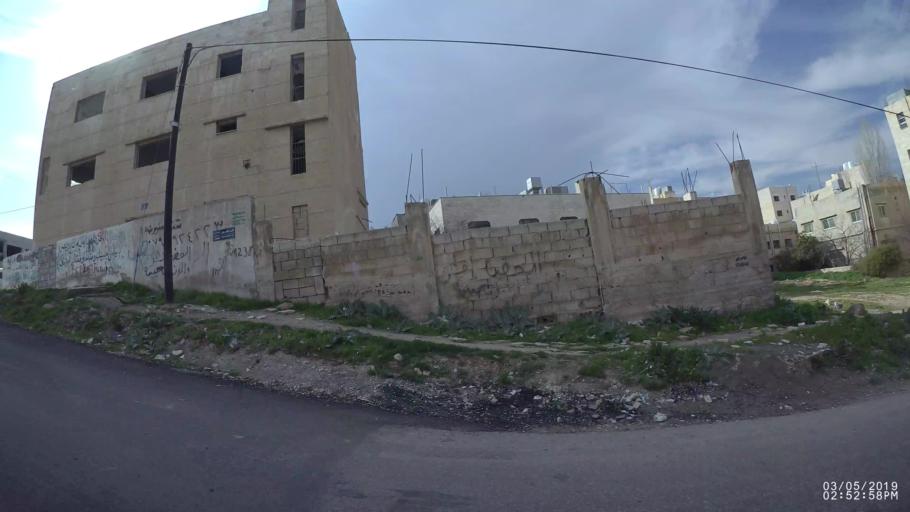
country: JO
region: Amman
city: Amman
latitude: 32.0086
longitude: 35.9520
